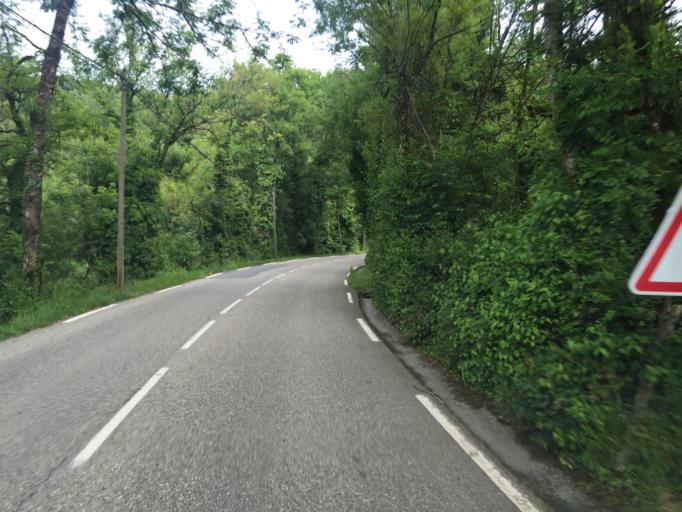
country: FR
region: Rhone-Alpes
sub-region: Departement de la Savoie
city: Jacob-Bellecombette
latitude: 45.5453
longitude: 5.9189
